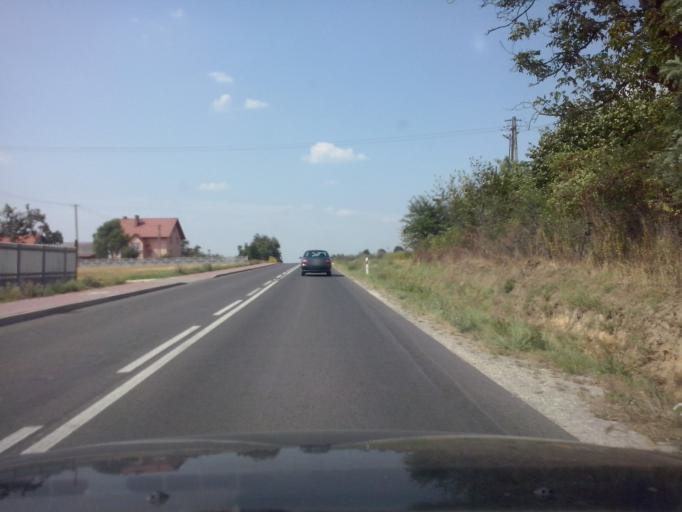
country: PL
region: Swietokrzyskie
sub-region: Powiat buski
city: Gnojno
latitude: 50.5868
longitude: 20.9136
